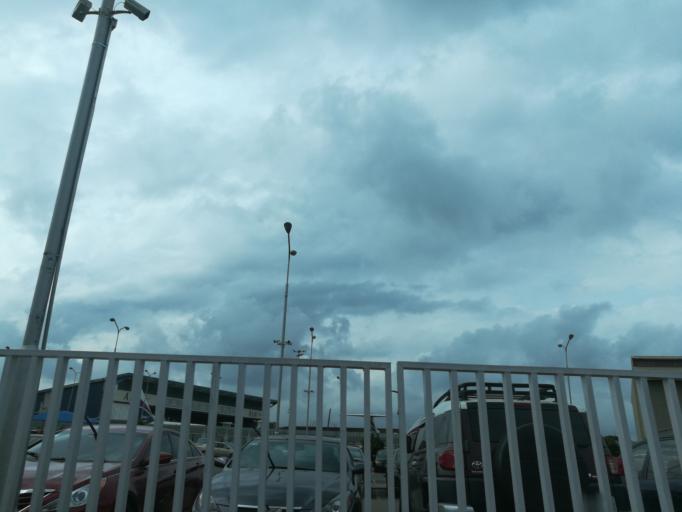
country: NG
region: Lagos
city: Ikeja
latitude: 6.5894
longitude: 3.3313
